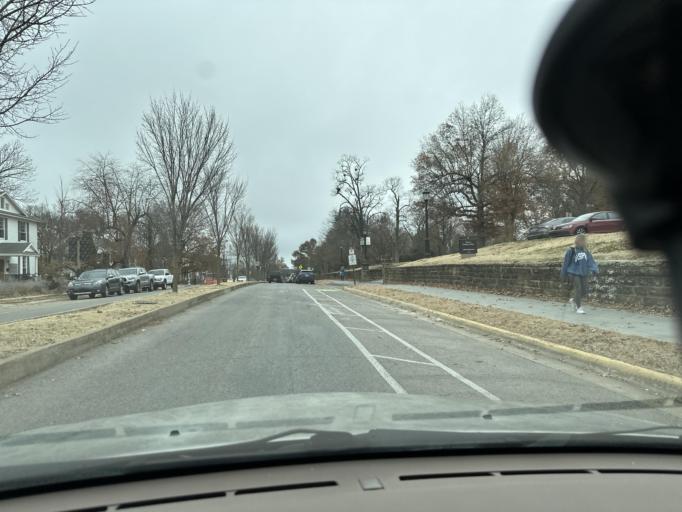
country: US
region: Arkansas
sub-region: Washington County
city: Fayetteville
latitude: 36.0698
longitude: -94.1685
